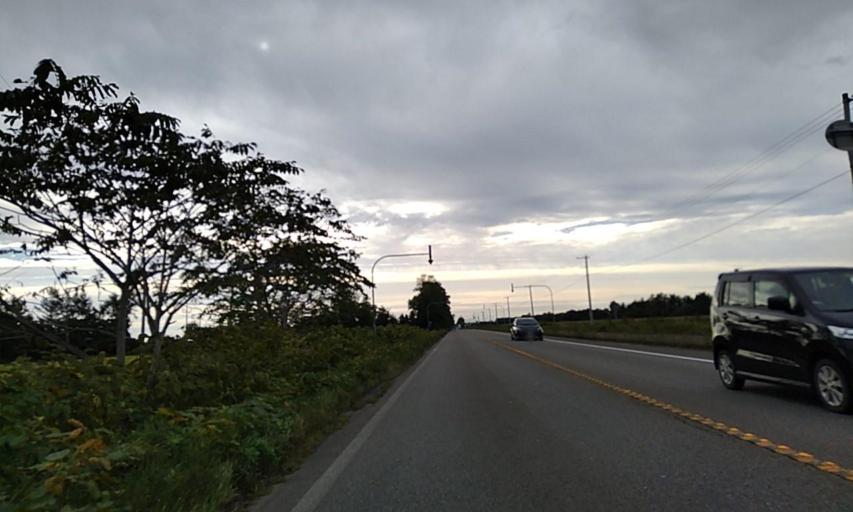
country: JP
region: Hokkaido
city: Obihiro
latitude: 42.9321
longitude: 142.9773
